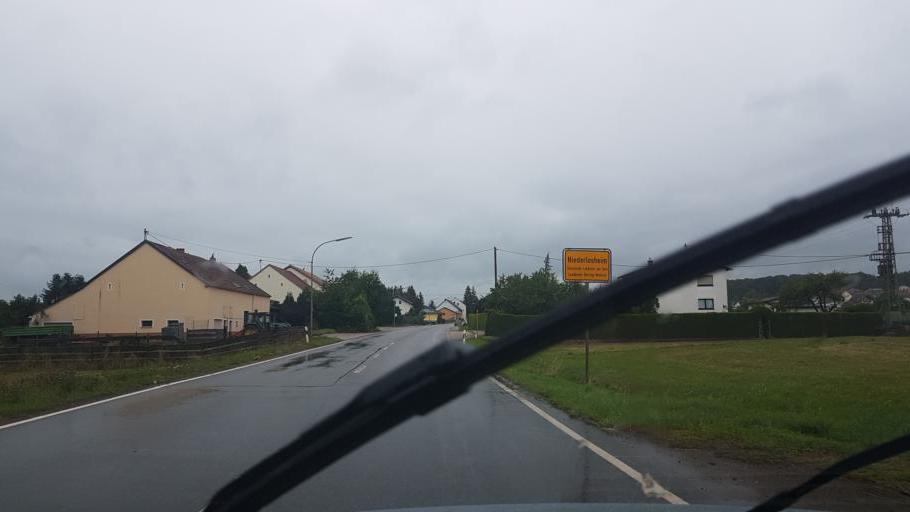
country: DE
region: Saarland
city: Losheim
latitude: 49.5029
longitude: 6.7865
